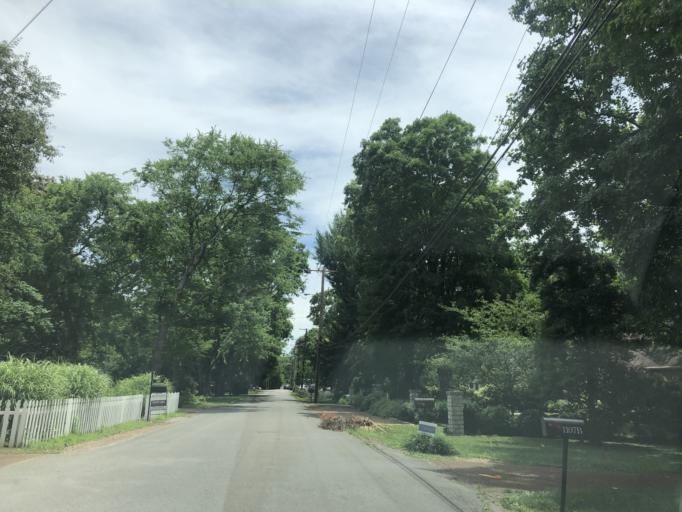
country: US
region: Tennessee
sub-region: Davidson County
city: Oak Hill
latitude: 36.1139
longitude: -86.7903
